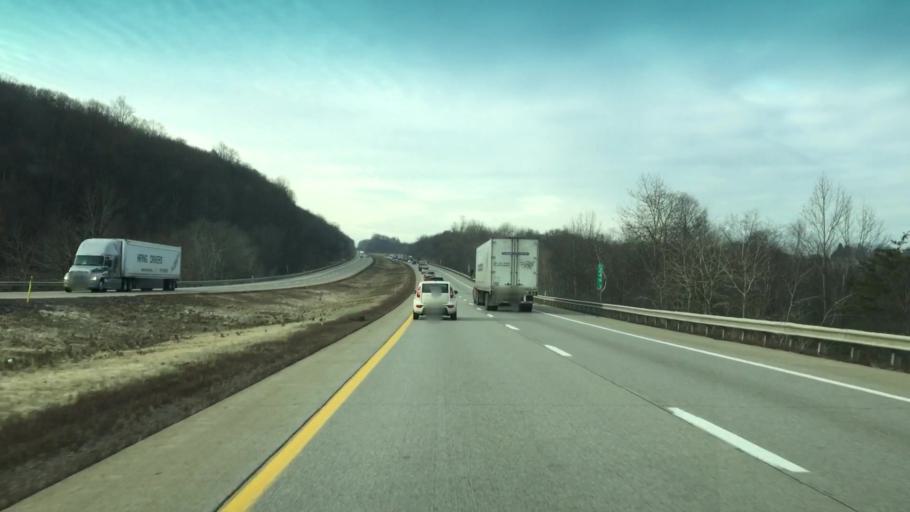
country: US
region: Pennsylvania
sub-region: Luzerne County
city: Nescopeck
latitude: 41.0187
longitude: -76.1852
